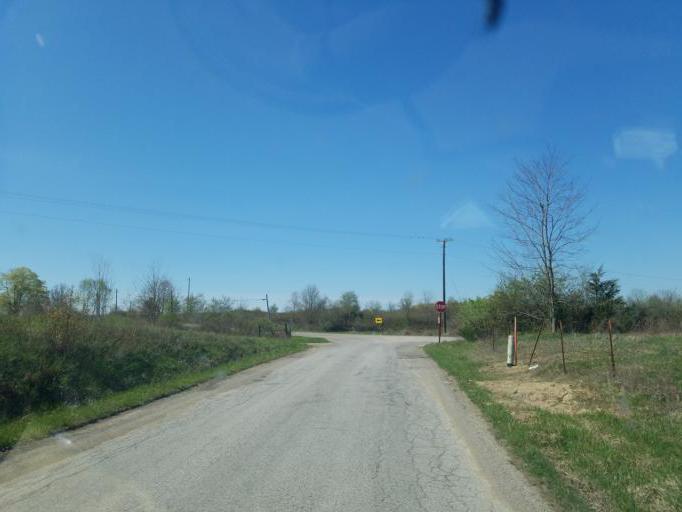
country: US
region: Ohio
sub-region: Morrow County
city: Mount Gilead
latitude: 40.5673
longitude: -82.8052
